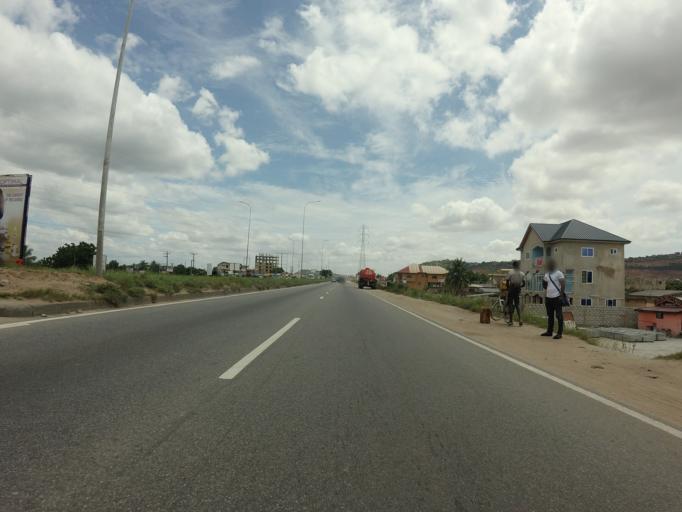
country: GH
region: Central
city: Kasoa
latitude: 5.5419
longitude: -0.3924
